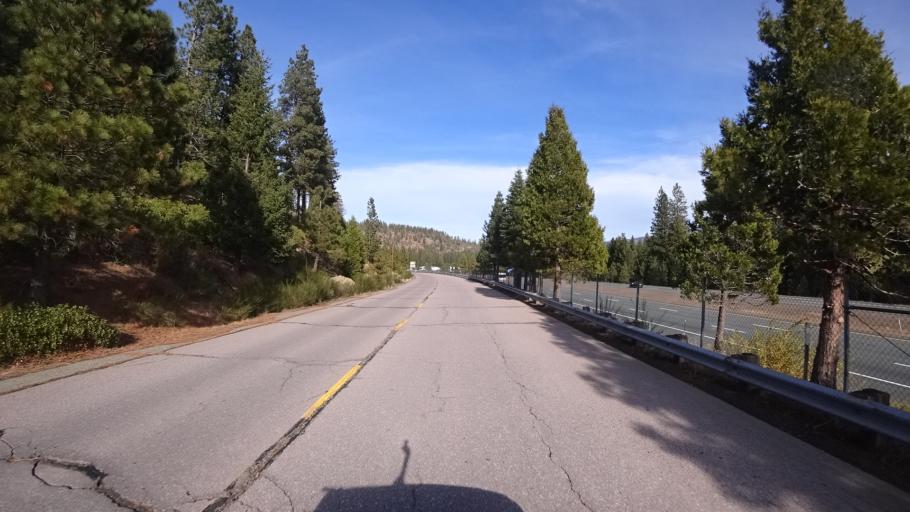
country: US
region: California
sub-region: Siskiyou County
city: Weed
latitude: 41.4061
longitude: -122.3817
